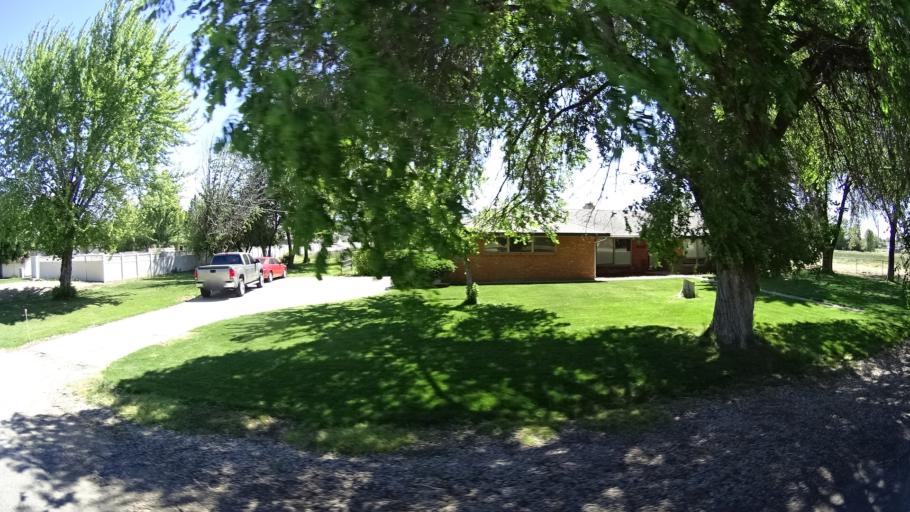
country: US
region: Idaho
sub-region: Ada County
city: Meridian
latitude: 43.6518
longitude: -116.3745
